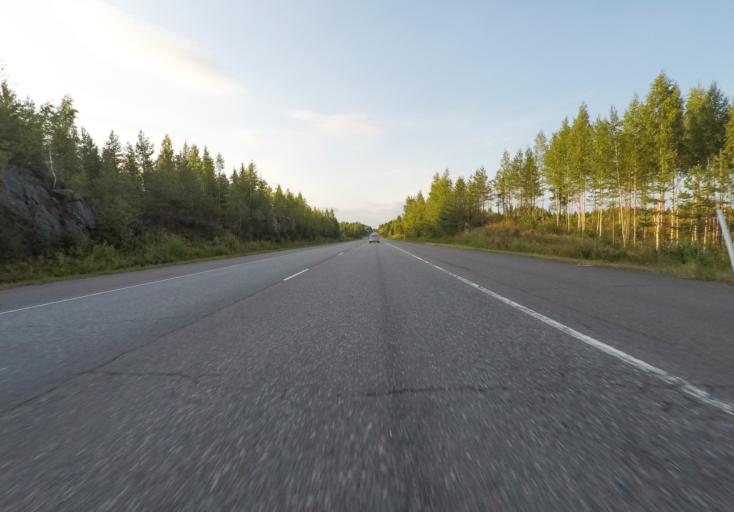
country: FI
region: Paijanne Tavastia
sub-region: Lahti
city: Heinola
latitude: 61.3171
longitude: 26.0433
